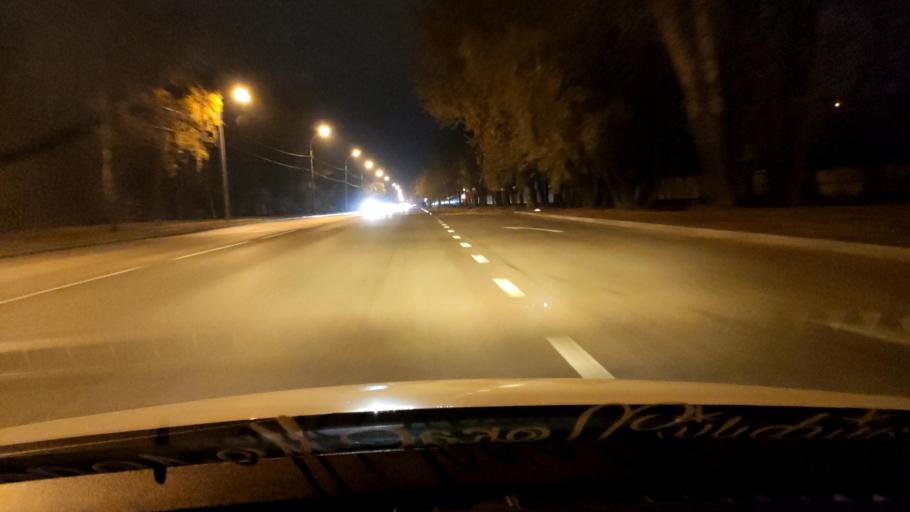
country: RU
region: Voronezj
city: Voronezh
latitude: 51.6501
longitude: 39.2115
